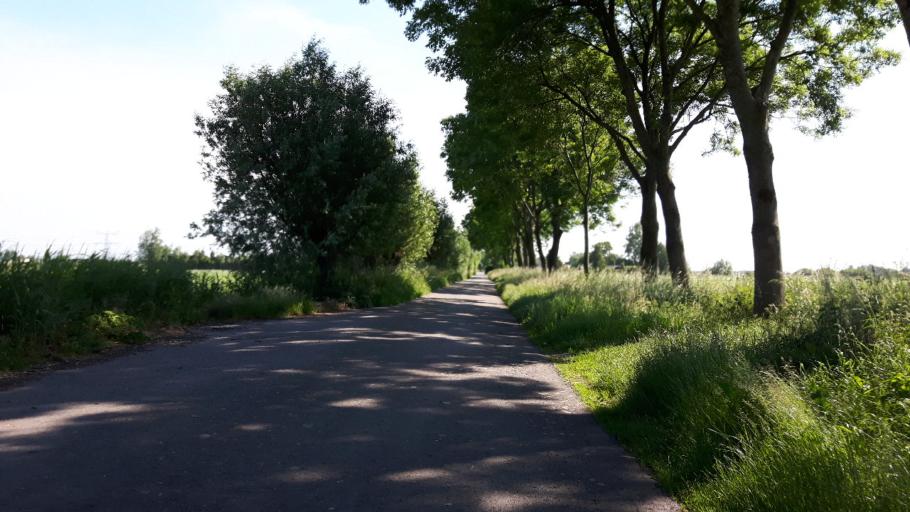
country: NL
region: Utrecht
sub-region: Stichtse Vecht
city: Breukelen
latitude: 52.2186
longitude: 4.9823
